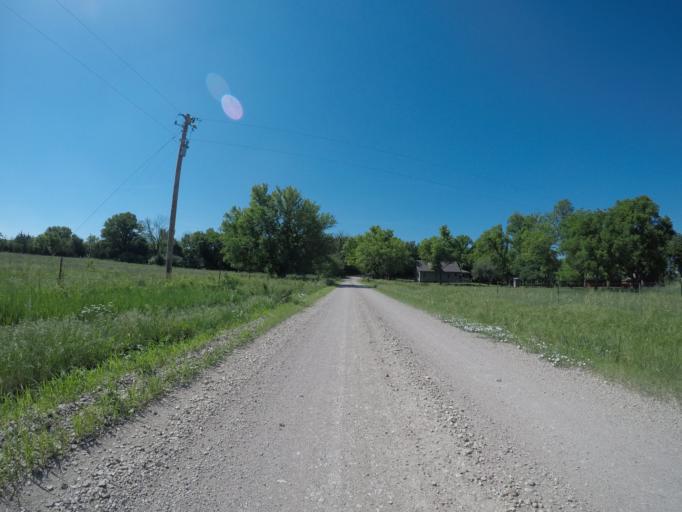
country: US
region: Kansas
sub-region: Wabaunsee County
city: Alma
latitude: 39.0203
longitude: -96.1506
